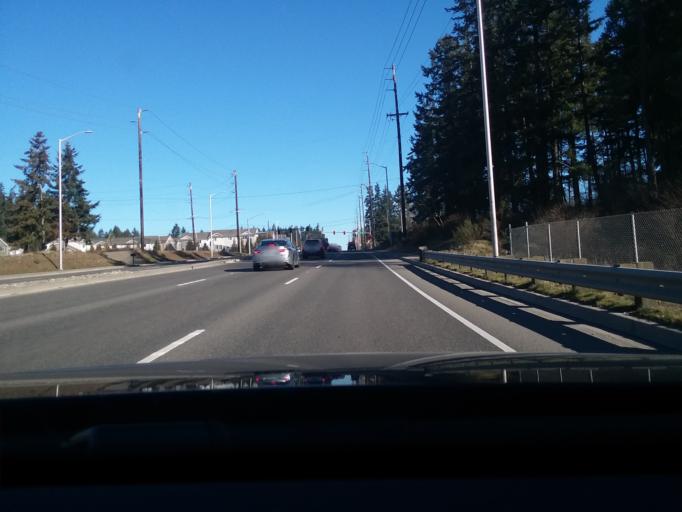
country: US
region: Washington
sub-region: Pierce County
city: Frederickson
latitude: 47.1039
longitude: -122.3575
